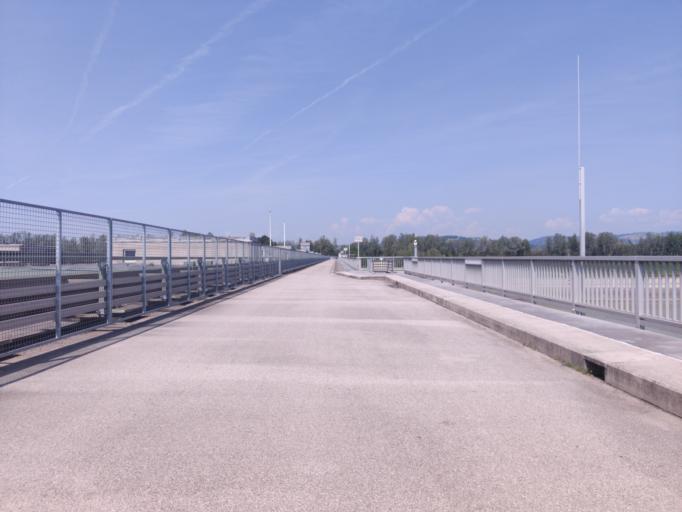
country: AT
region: Upper Austria
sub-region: Politischer Bezirk Urfahr-Umgebung
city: Ottensheim
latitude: 48.3170
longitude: 14.1511
